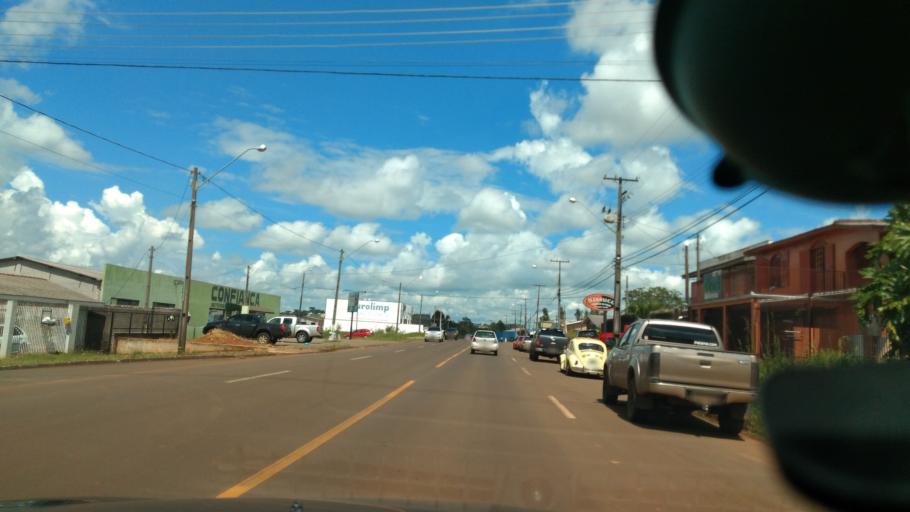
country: BR
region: Parana
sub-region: Guarapuava
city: Guarapuava
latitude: -25.3930
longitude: -51.4956
